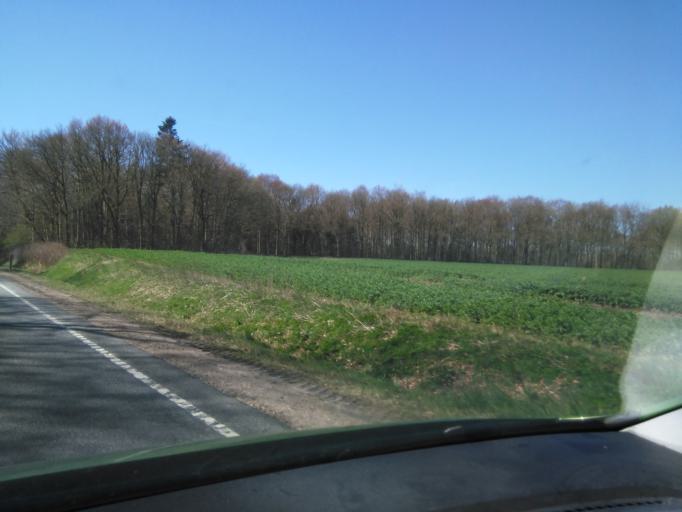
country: DK
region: South Denmark
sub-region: Varde Kommune
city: Olgod
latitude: 55.6886
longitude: 8.6015
